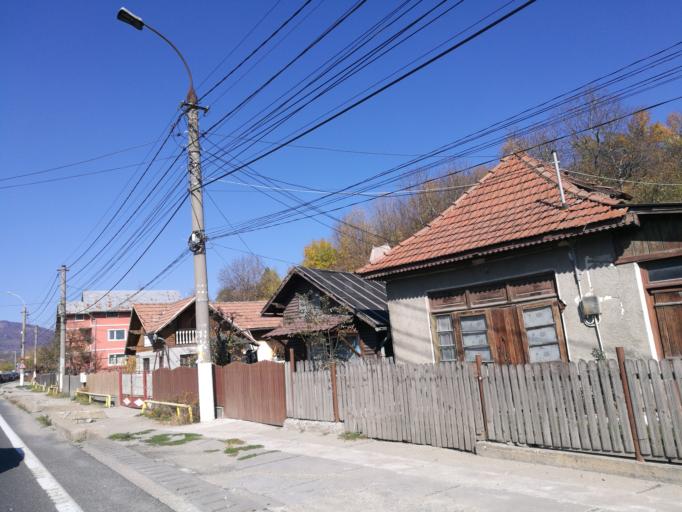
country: RO
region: Prahova
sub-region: Oras Breaza
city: Gura Beliei
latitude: 45.2268
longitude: 25.6395
